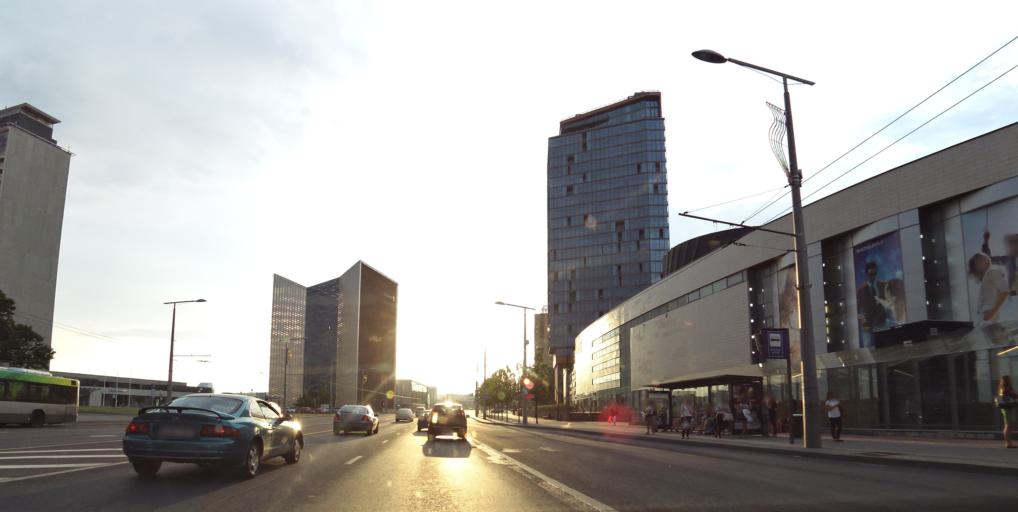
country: LT
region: Vilnius County
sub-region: Vilnius
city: Vilnius
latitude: 54.6955
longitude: 25.2777
